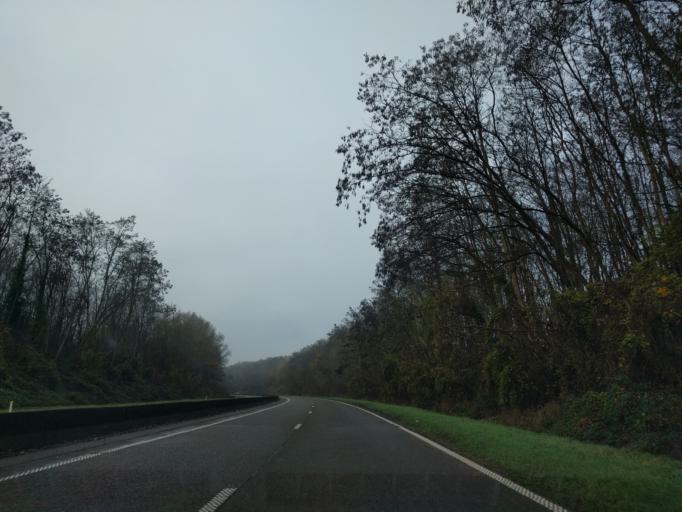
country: BE
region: Wallonia
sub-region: Province de Namur
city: Dinant
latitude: 50.2442
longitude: 4.9023
